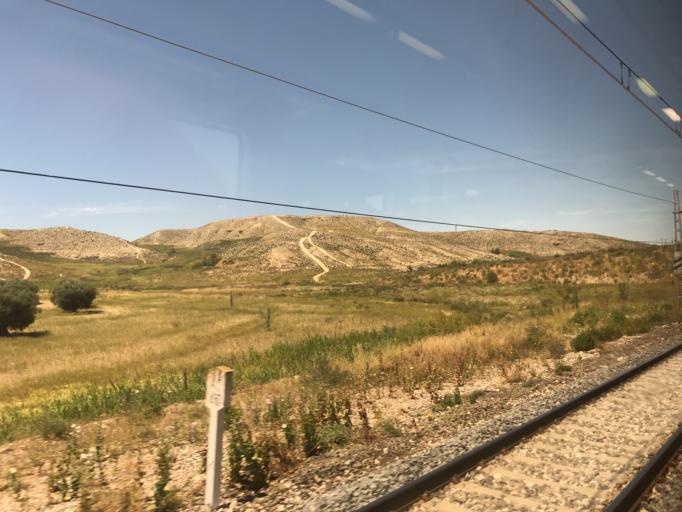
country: ES
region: Madrid
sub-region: Provincia de Madrid
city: Ciempozuelos
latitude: 40.1370
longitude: -3.6125
